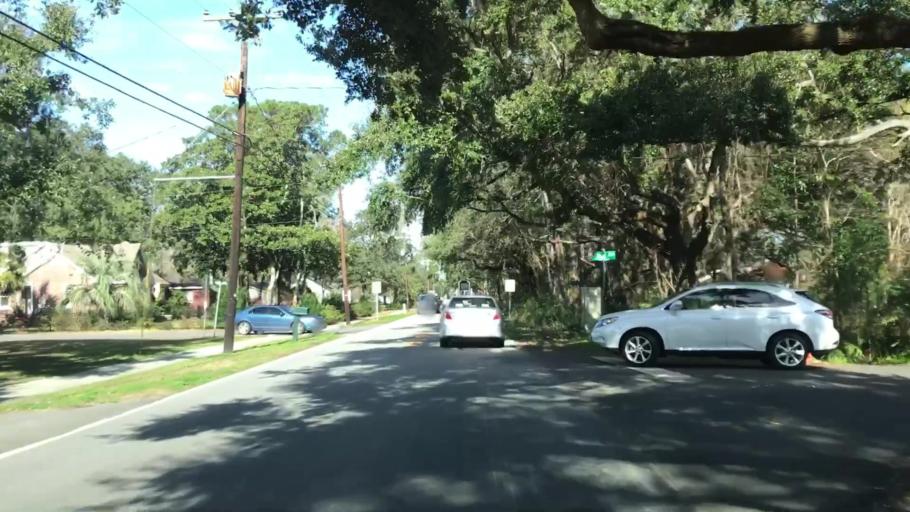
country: US
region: South Carolina
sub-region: Charleston County
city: North Charleston
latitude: 32.7820
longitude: -80.0199
